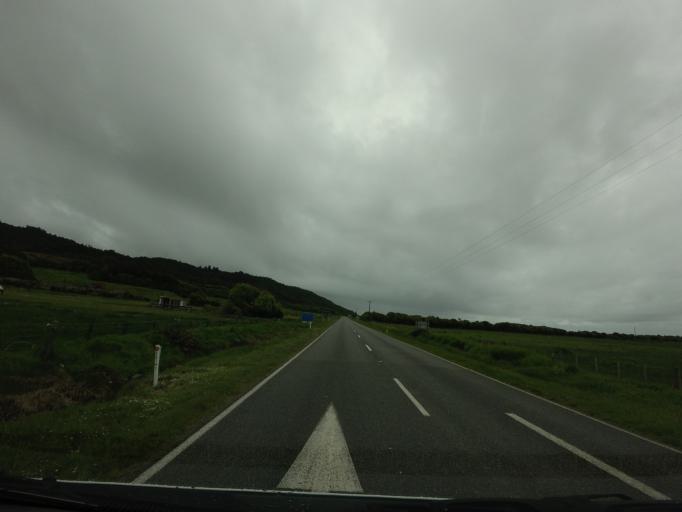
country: NZ
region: West Coast
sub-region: Westland District
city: Hokitika
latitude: -42.8932
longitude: 170.8095
